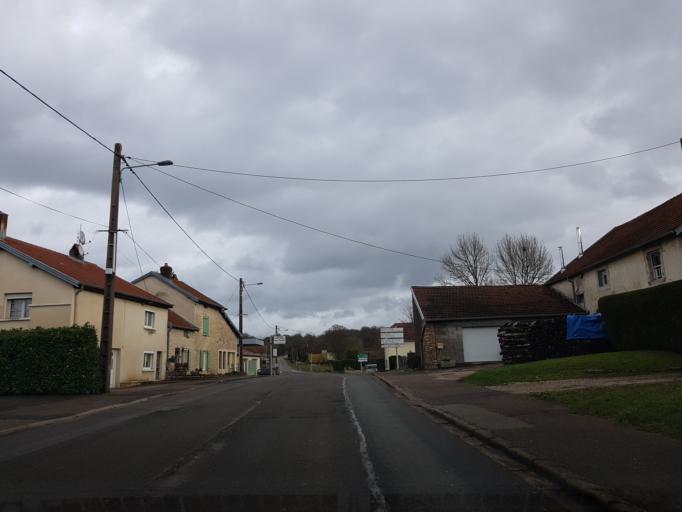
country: FR
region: Franche-Comte
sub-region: Departement de la Haute-Saone
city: Scey-sur-Saone-et-Saint-Albin
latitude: 47.7089
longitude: 5.8966
